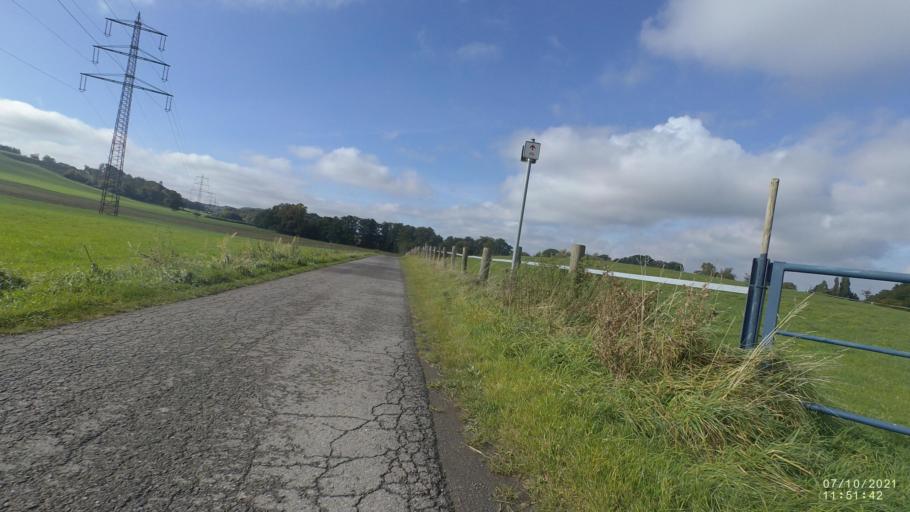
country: DE
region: North Rhine-Westphalia
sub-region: Regierungsbezirk Arnsberg
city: Menden
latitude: 51.4294
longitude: 7.7434
